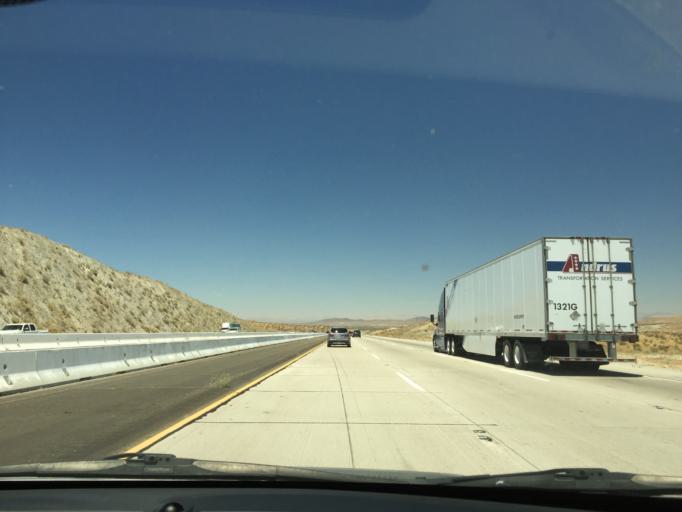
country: US
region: California
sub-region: San Bernardino County
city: Victorville
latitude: 34.6776
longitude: -117.2116
